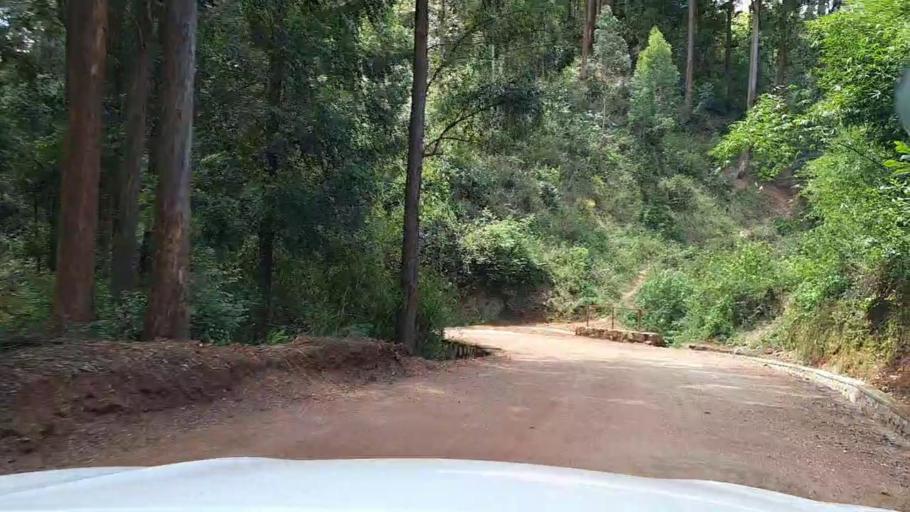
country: BI
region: Ngozi
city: Ngozi
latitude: -2.8131
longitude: 29.7292
